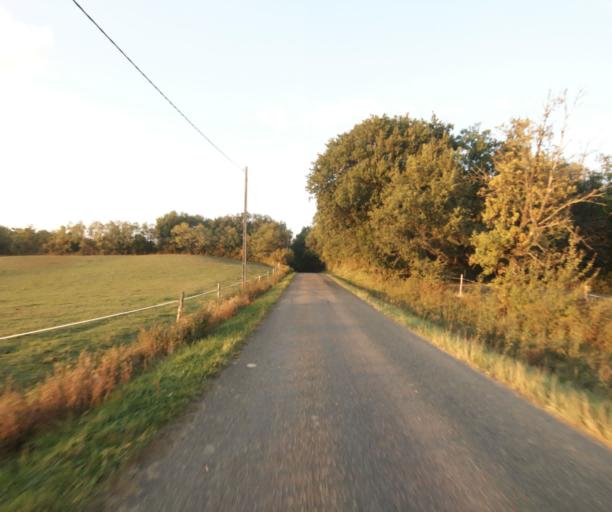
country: FR
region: Midi-Pyrenees
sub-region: Departement du Gers
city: Vic-Fezensac
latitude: 43.7879
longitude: 0.2235
